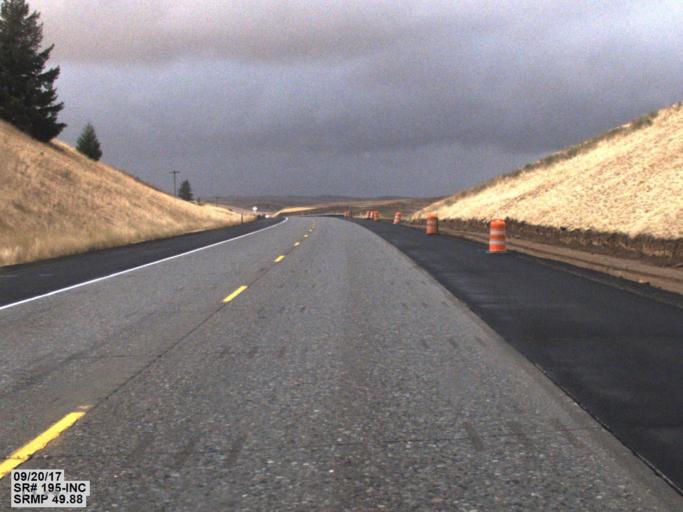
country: US
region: Washington
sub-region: Whitman County
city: Colfax
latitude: 47.0322
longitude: -117.3640
